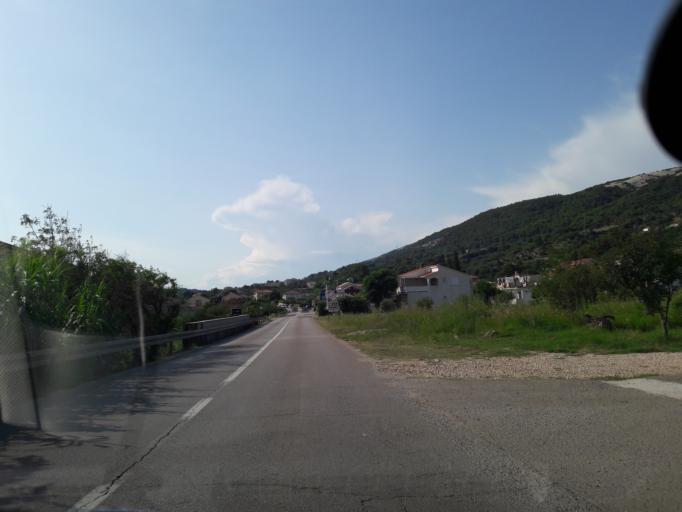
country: HR
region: Primorsko-Goranska
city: Banjol
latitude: 44.7465
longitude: 14.7900
